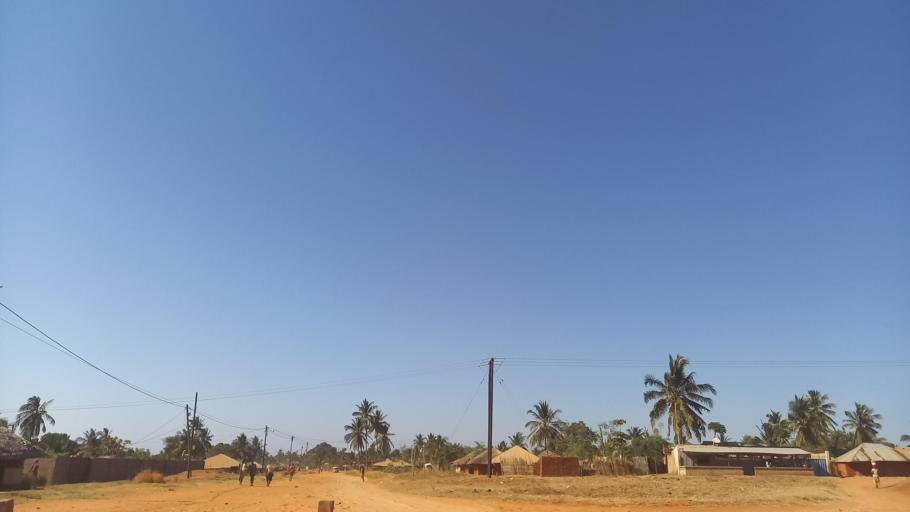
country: MZ
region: Cabo Delgado
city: Pemba
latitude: -13.1352
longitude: 40.5489
